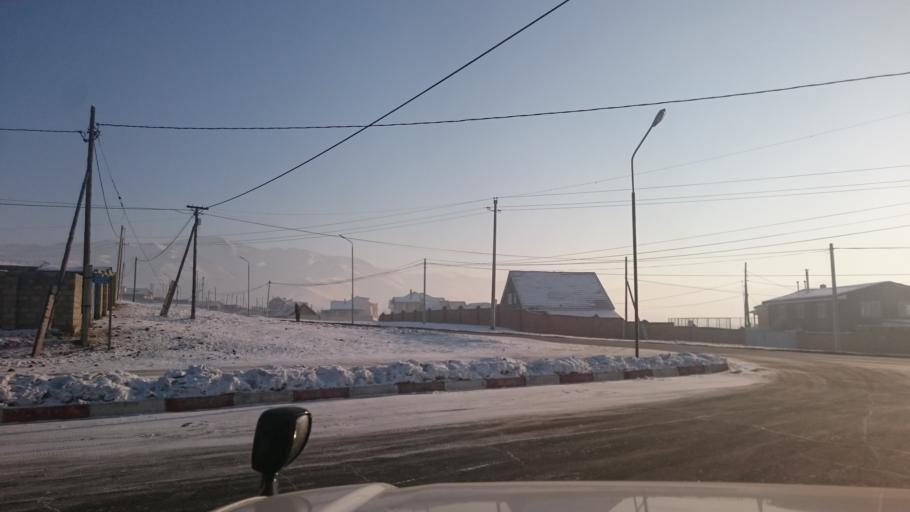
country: MN
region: Ulaanbaatar
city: Ulaanbaatar
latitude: 47.9286
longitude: 107.1462
